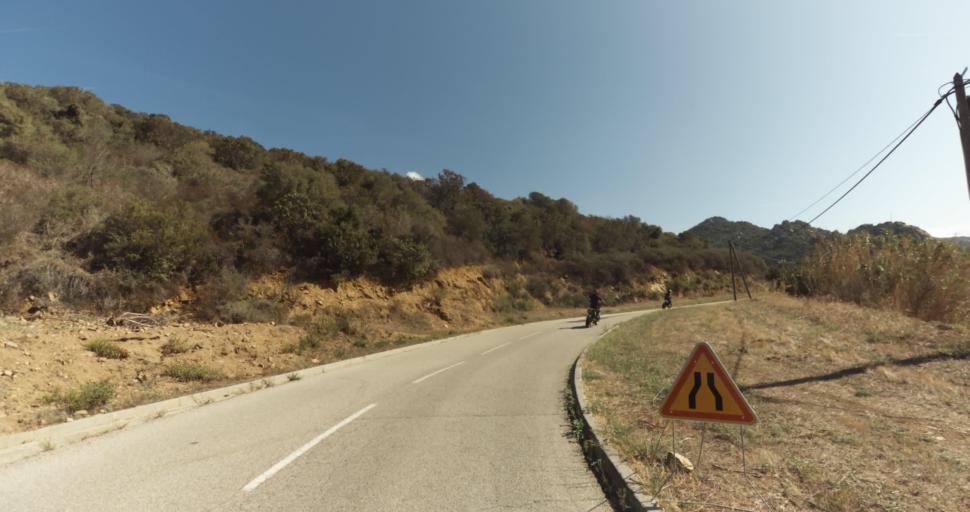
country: FR
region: Corsica
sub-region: Departement de la Corse-du-Sud
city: Ajaccio
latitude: 41.9184
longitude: 8.6414
